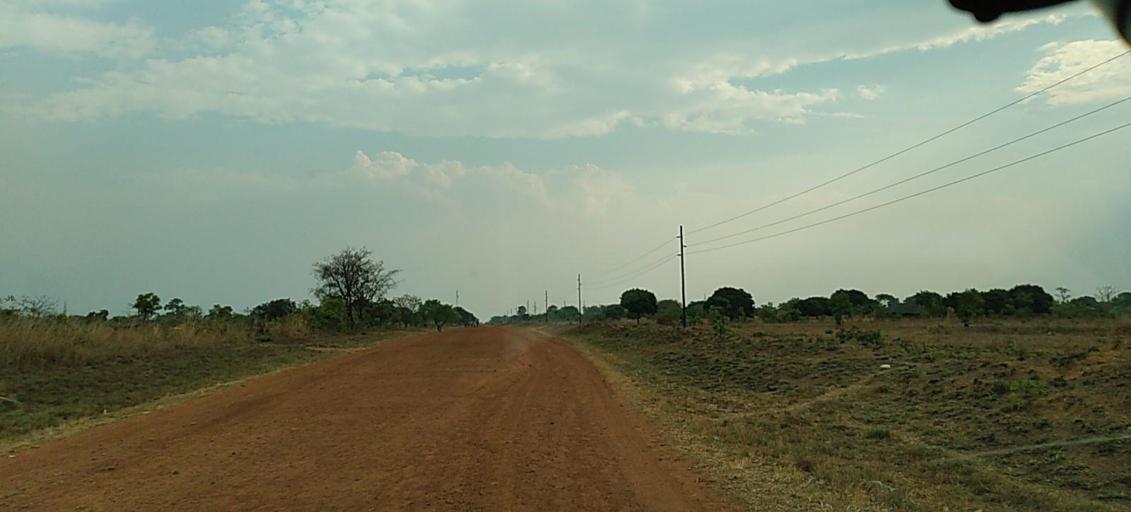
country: ZM
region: North-Western
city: Kabompo
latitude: -13.8697
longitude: 23.6685
